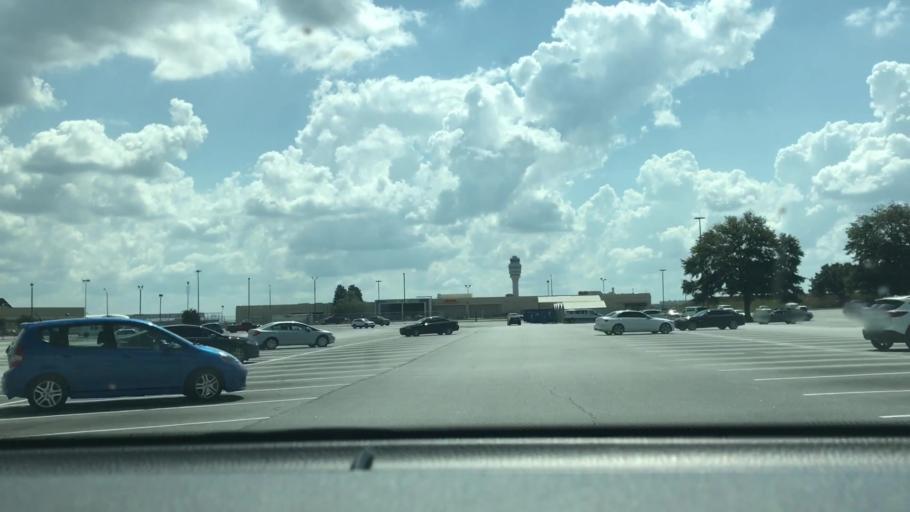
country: US
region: Georgia
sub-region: Fulton County
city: Hapeville
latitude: 33.6553
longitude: -84.4217
